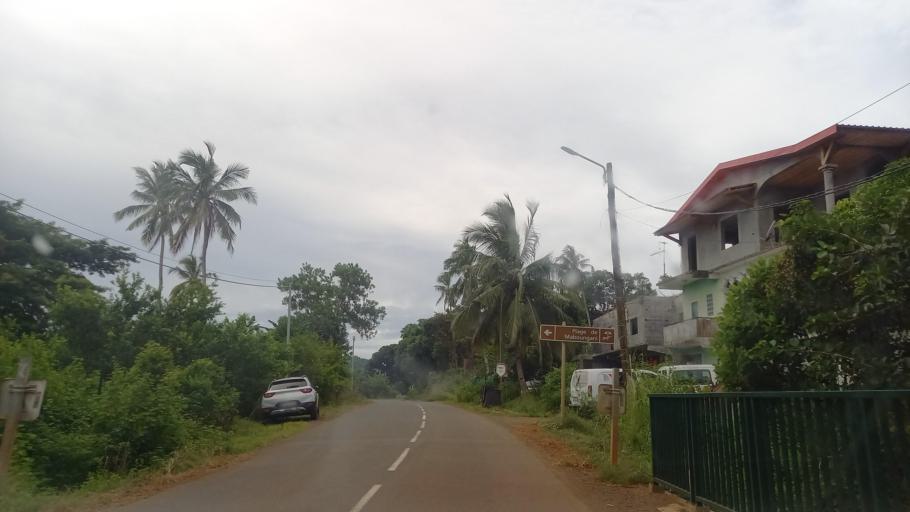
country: YT
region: Kani-Keli
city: Kani Keli
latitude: -12.9392
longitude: 45.1022
